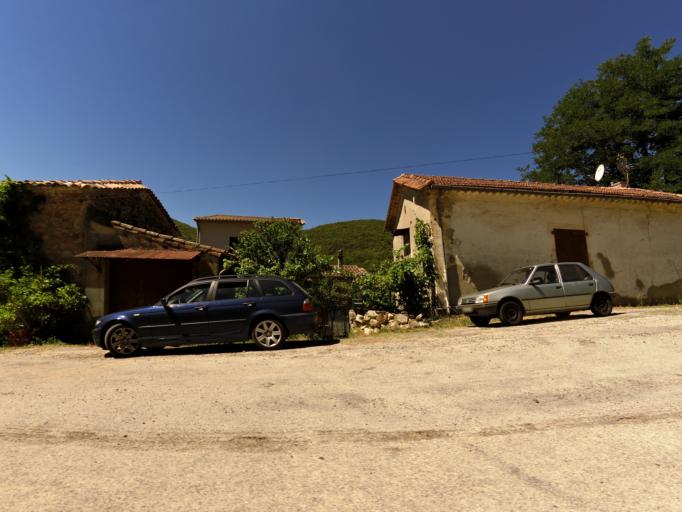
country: FR
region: Languedoc-Roussillon
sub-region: Departement du Gard
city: Saint-Jean-du-Gard
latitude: 44.0855
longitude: 3.9192
